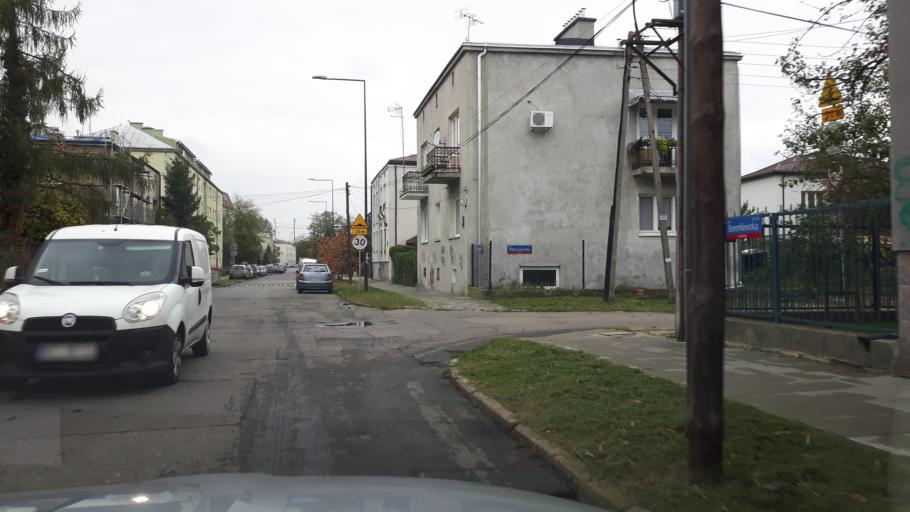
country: PL
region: Masovian Voivodeship
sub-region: Warszawa
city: Praga Poludnie
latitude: 52.2479
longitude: 21.1049
